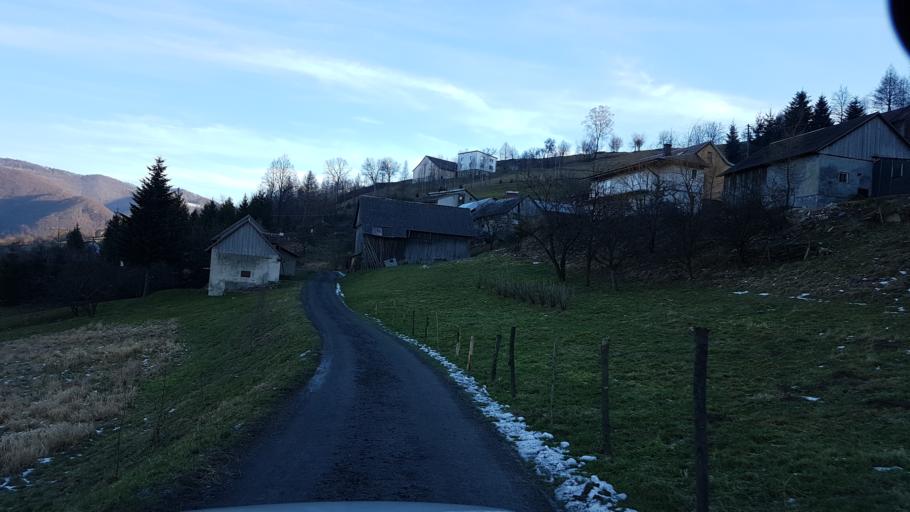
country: PL
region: Lesser Poland Voivodeship
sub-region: Powiat nowosadecki
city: Rytro
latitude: 49.4964
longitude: 20.6643
